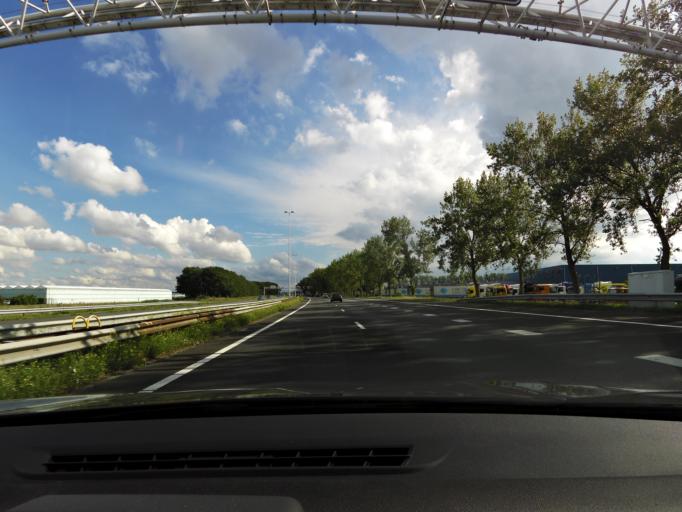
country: NL
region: South Holland
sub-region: Gemeente Westland
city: Maasdijk
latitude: 51.9481
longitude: 4.2345
